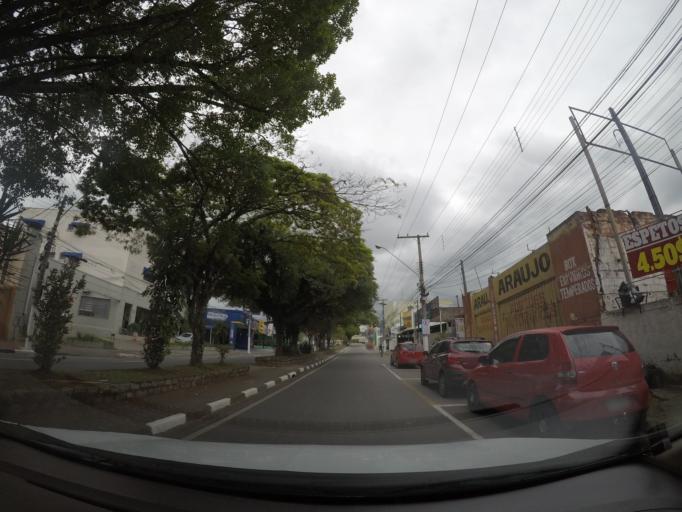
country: BR
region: Sao Paulo
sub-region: Aruja
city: Aruja
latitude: -23.3990
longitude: -46.3192
